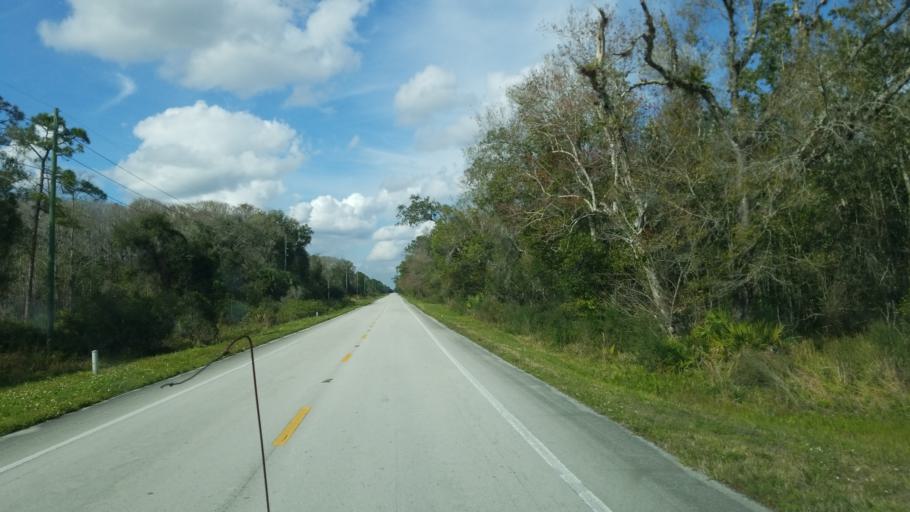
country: US
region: Florida
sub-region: Brevard County
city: June Park
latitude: 27.9643
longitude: -81.0052
